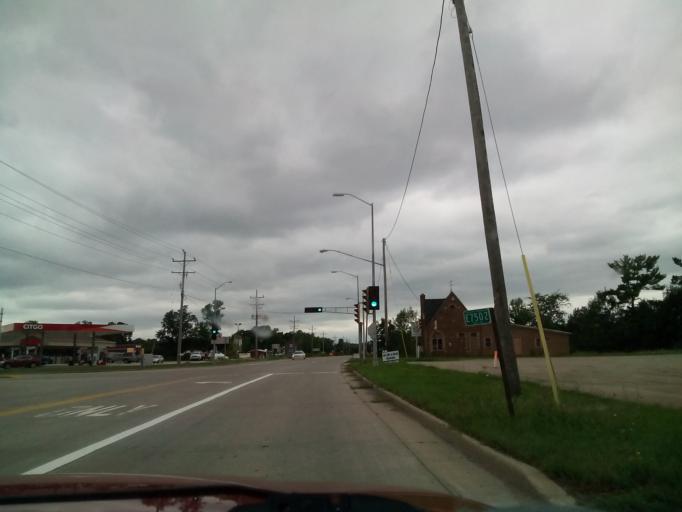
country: US
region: Wisconsin
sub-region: Waupaca County
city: Weyauwega
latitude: 44.2603
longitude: -88.8495
